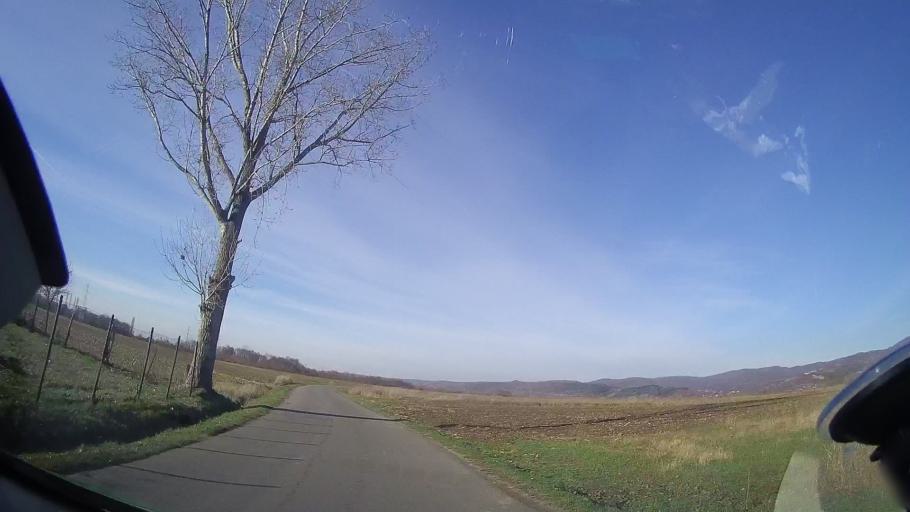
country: RO
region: Bihor
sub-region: Comuna Auseu
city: Auseu
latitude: 47.0268
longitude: 22.4855
